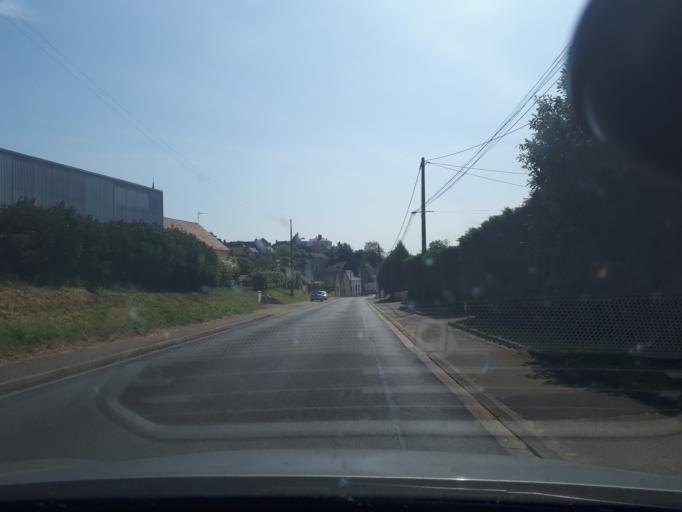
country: FR
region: Pays de la Loire
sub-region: Departement de la Sarthe
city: Montfort-le-Gesnois
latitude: 48.0498
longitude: 0.3987
